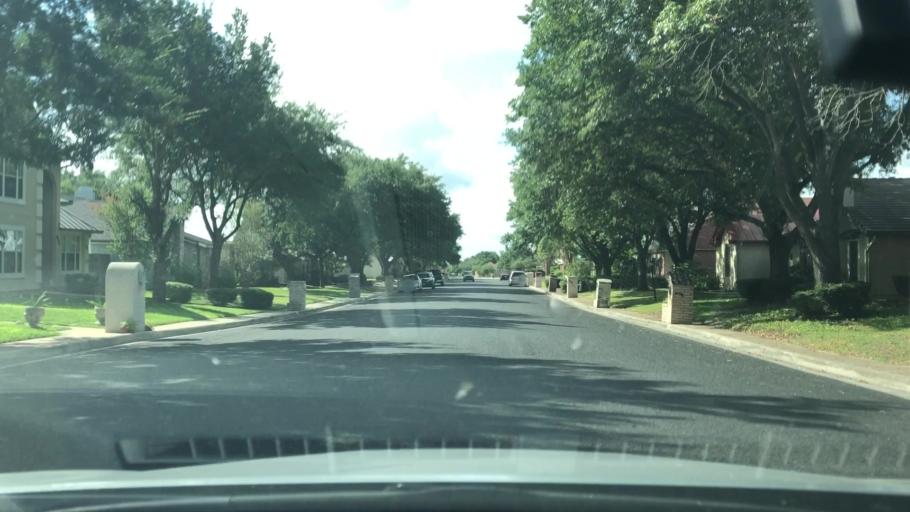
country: US
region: Texas
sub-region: Bexar County
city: Converse
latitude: 29.4889
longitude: -98.3379
